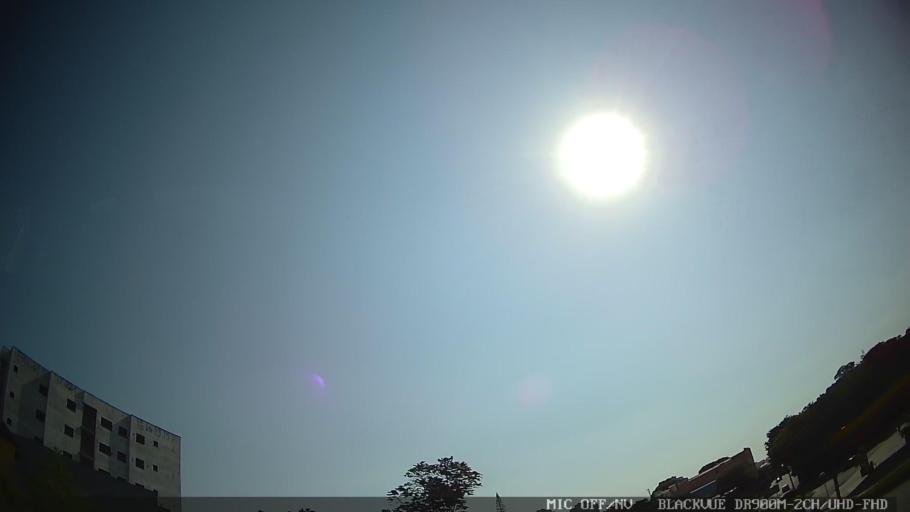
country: BR
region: Sao Paulo
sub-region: Itatiba
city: Itatiba
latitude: -23.0025
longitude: -46.8538
